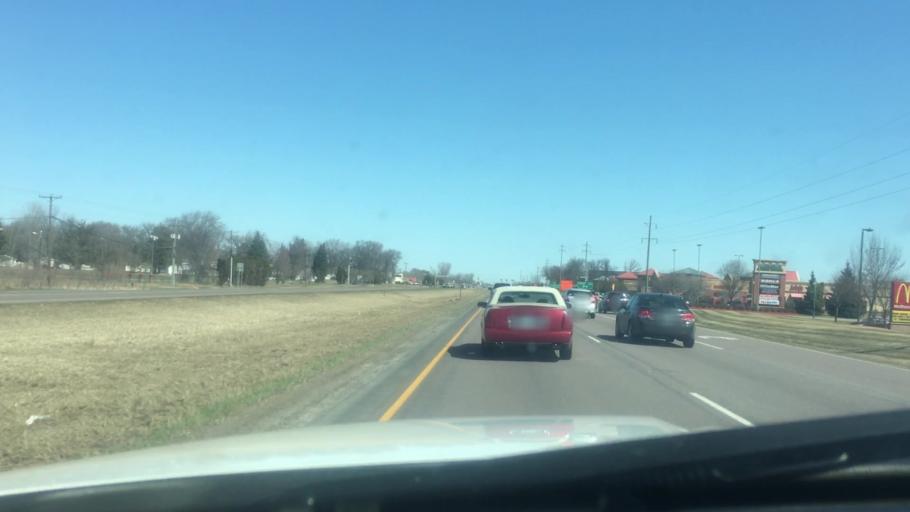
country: US
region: Minnesota
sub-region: Anoka County
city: Blaine
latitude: 45.1563
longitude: -93.2350
